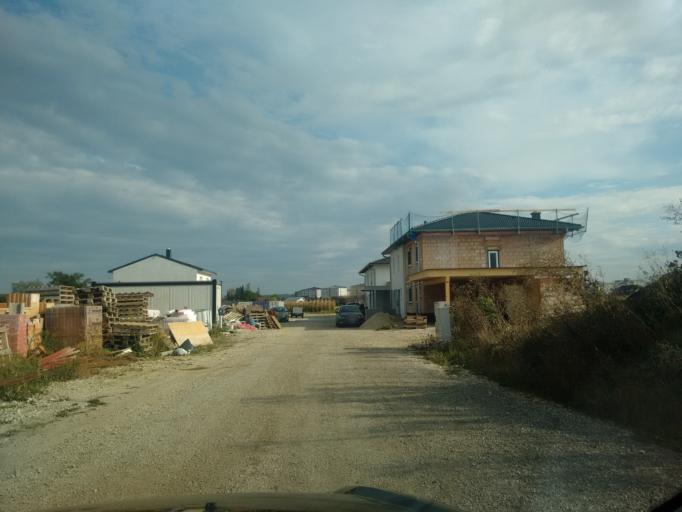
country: AT
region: Upper Austria
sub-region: Wels Stadt
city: Wels
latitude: 48.1663
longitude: 13.9910
